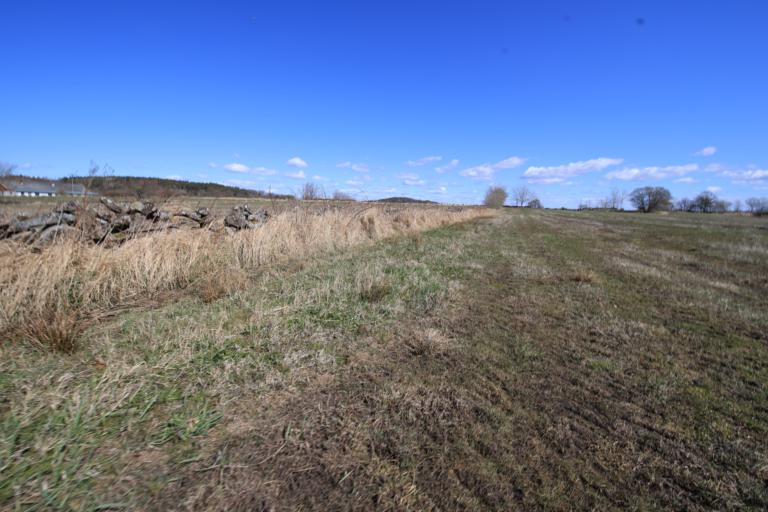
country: SE
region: Halland
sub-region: Varbergs Kommun
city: Varberg
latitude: 57.1572
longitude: 12.2621
